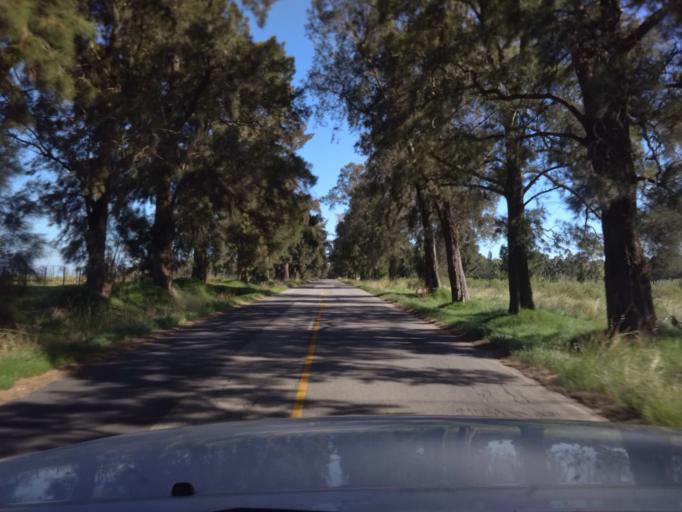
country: UY
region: Canelones
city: San Bautista
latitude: -34.3846
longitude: -55.9595
